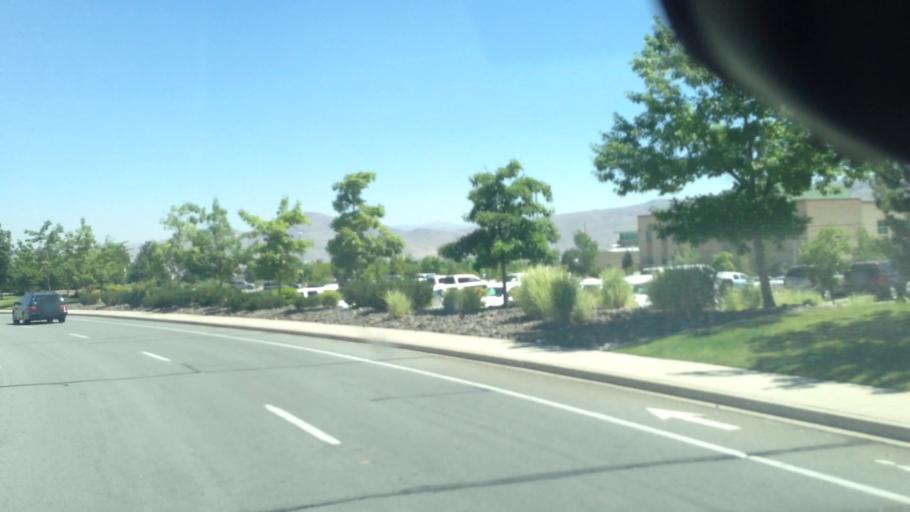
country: US
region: Nevada
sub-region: Storey County
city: Virginia City
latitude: 39.3909
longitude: -119.7672
